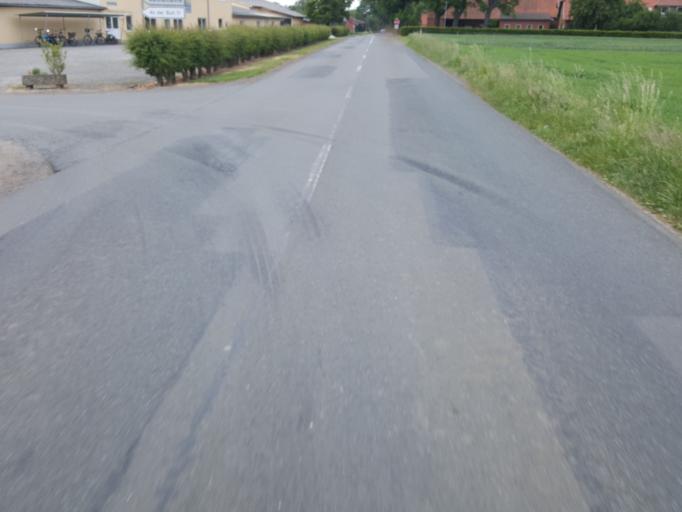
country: DE
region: Lower Saxony
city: Stolzenau
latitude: 52.5156
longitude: 9.0591
